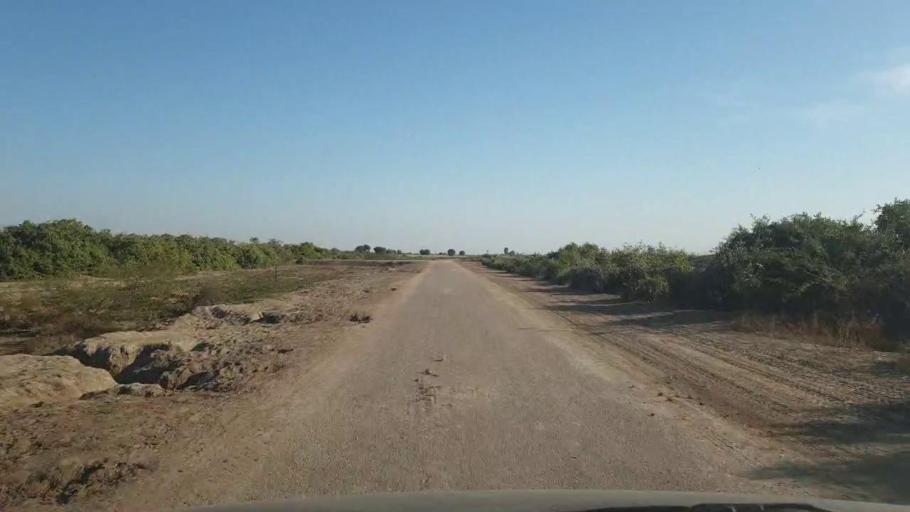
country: PK
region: Sindh
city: Dhoro Naro
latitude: 25.4264
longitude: 69.5336
